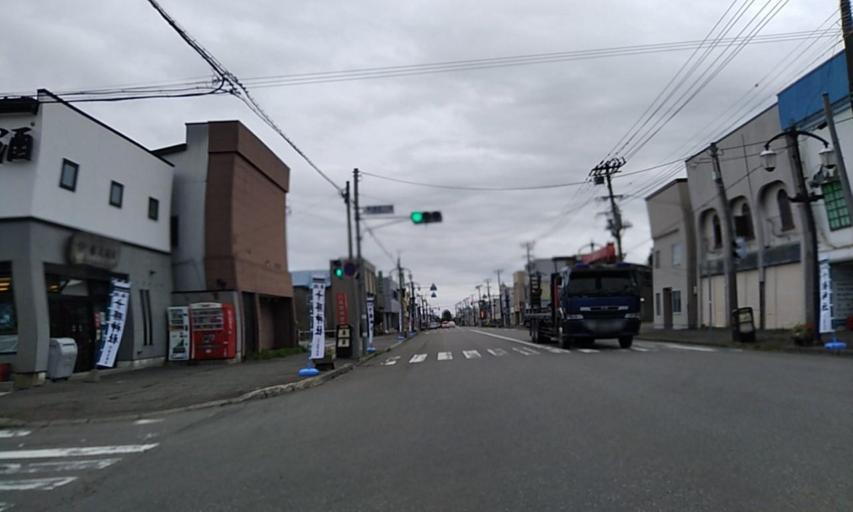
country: JP
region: Hokkaido
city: Obihiro
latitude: 42.2887
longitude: 143.3154
